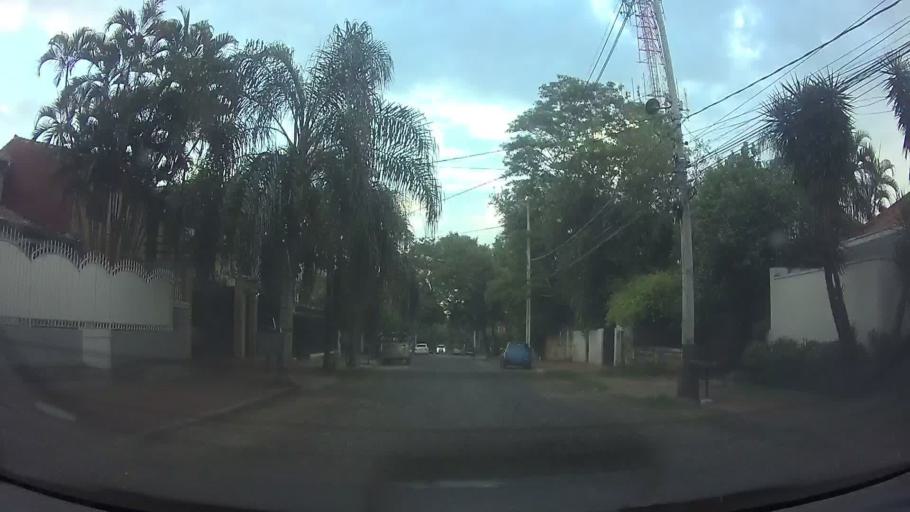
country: PY
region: Asuncion
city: Asuncion
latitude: -25.2667
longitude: -57.5700
